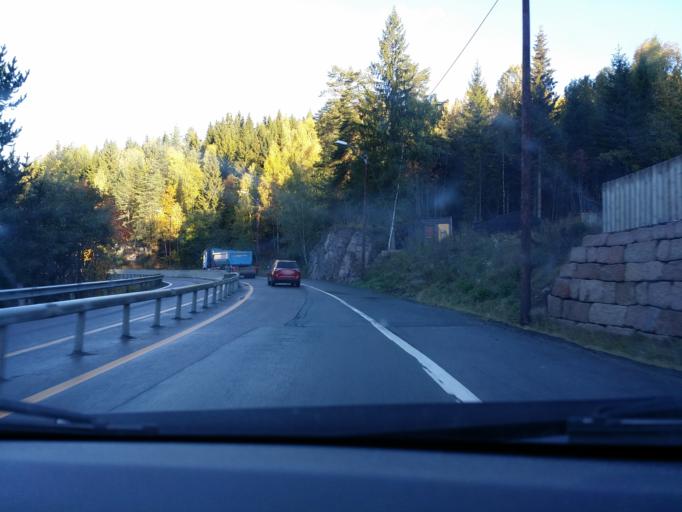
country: NO
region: Buskerud
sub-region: Hole
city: Vik
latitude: 59.9750
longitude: 10.3327
